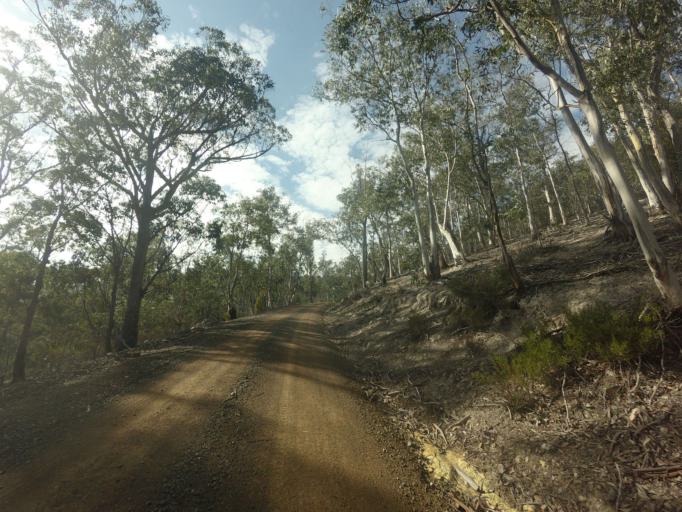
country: AU
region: Tasmania
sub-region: Sorell
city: Sorell
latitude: -42.5277
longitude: 147.4558
